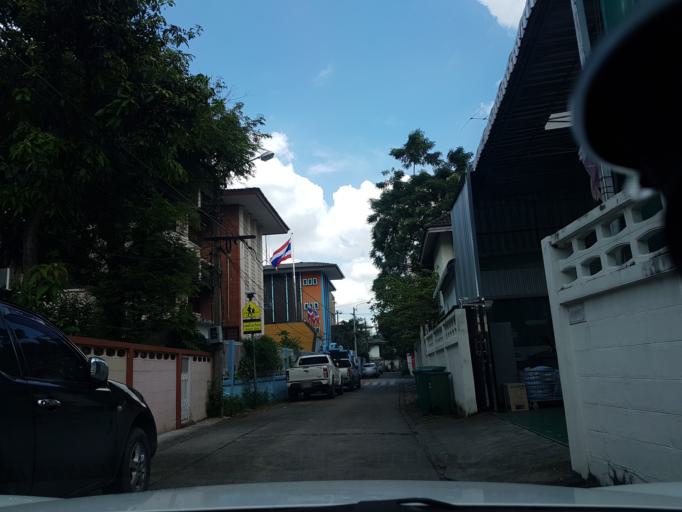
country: TH
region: Bangkok
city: Watthana
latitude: 13.7203
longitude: 100.5933
